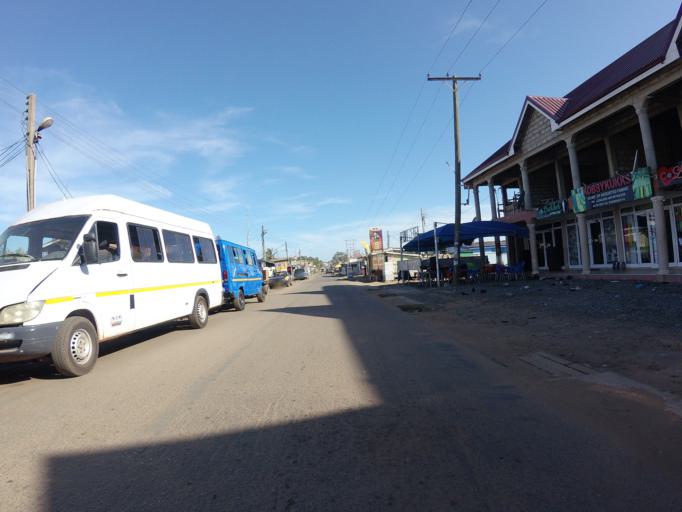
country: GH
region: Greater Accra
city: Nungua
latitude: 5.5940
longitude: -0.0844
